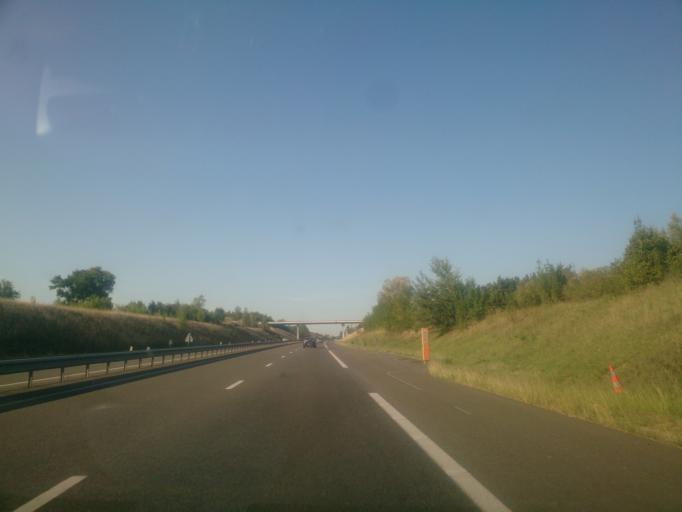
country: FR
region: Midi-Pyrenees
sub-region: Departement du Tarn-et-Garonne
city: Caussade
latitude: 44.1905
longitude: 1.5361
